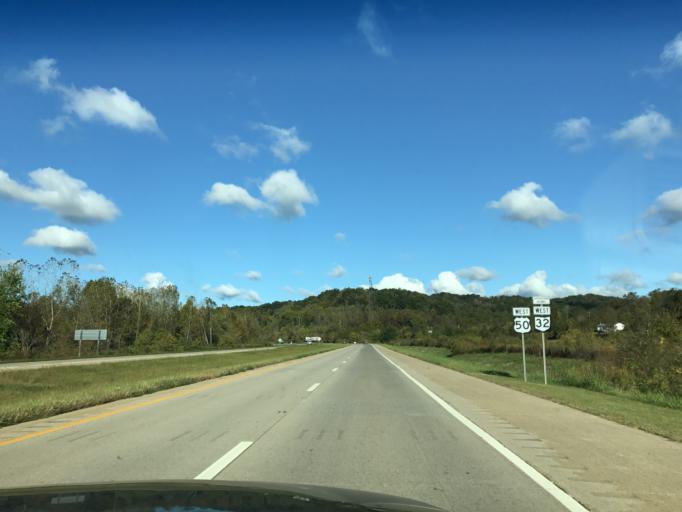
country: US
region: Ohio
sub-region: Athens County
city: Athens
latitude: 39.3303
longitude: -82.0031
